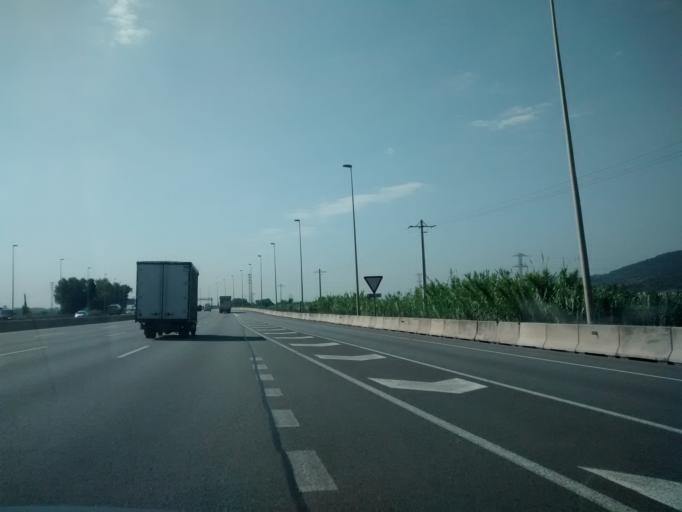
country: ES
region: Catalonia
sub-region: Provincia de Barcelona
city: Molins de Rei
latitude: 41.4046
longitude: 2.0169
